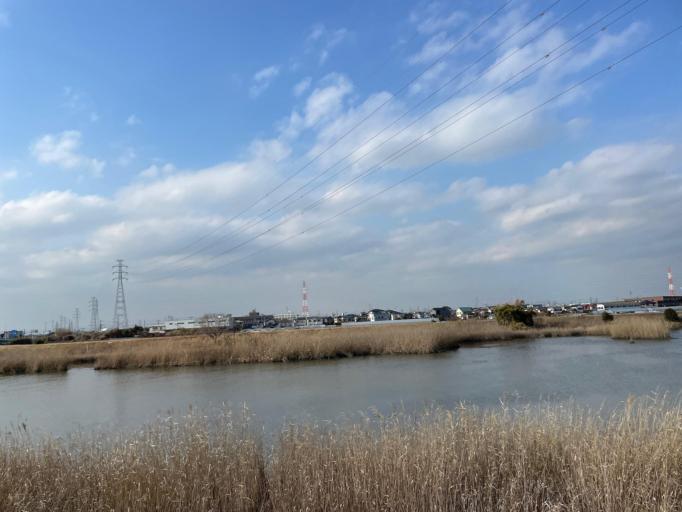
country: JP
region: Saitama
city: Yashio-shi
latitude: 35.8087
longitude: 139.8640
